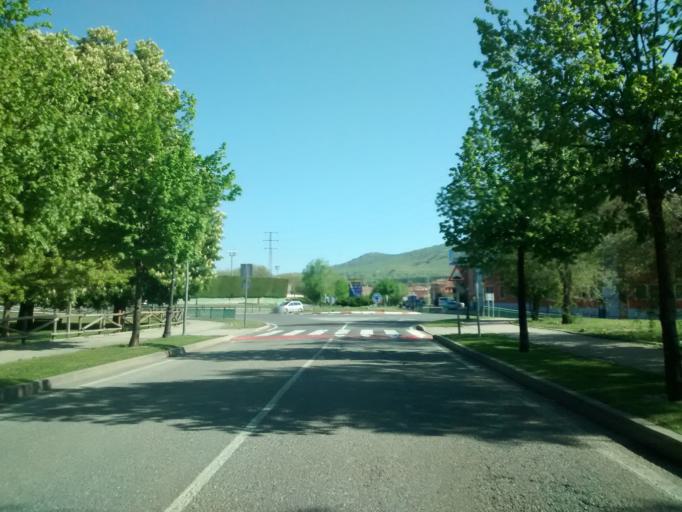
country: ES
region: Castille and Leon
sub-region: Provincia de Segovia
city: San Ildefonso
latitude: 40.9051
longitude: -4.0089
